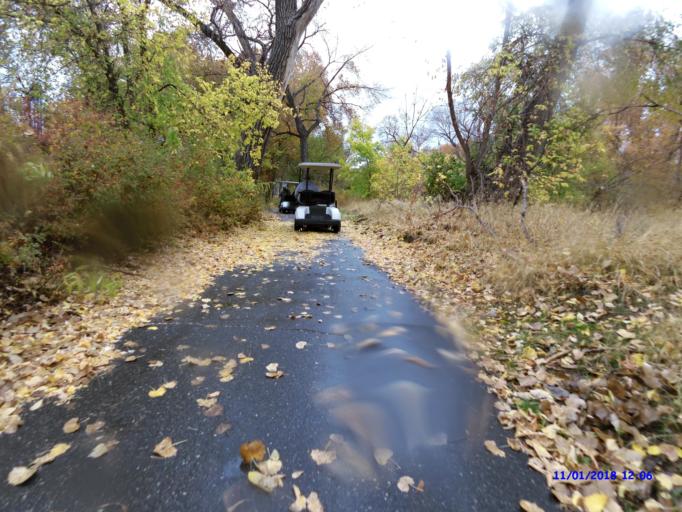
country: US
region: Utah
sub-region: Weber County
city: Ogden
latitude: 41.2290
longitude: -111.9938
